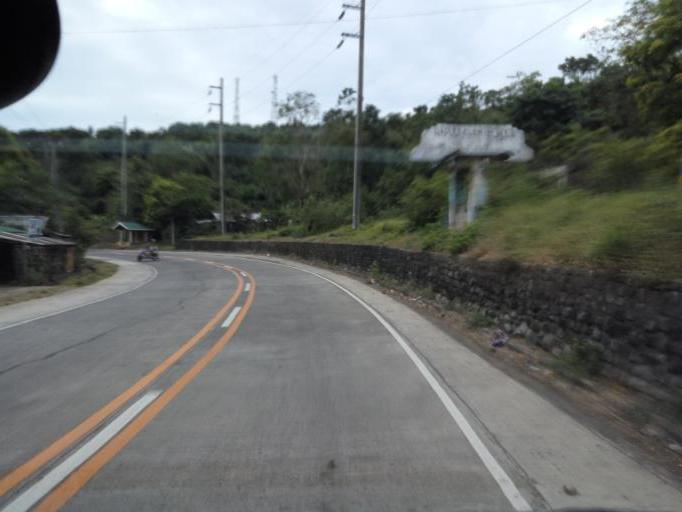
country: PH
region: Cagayan Valley
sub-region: Province of Cagayan
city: Casambalangan
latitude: 18.3962
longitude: 122.1318
